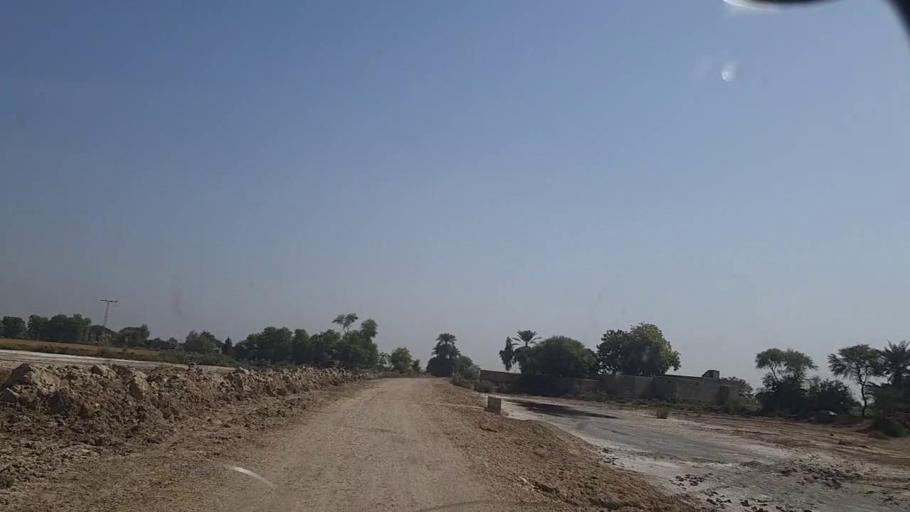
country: PK
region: Sindh
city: Thul
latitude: 28.1128
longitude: 68.7245
